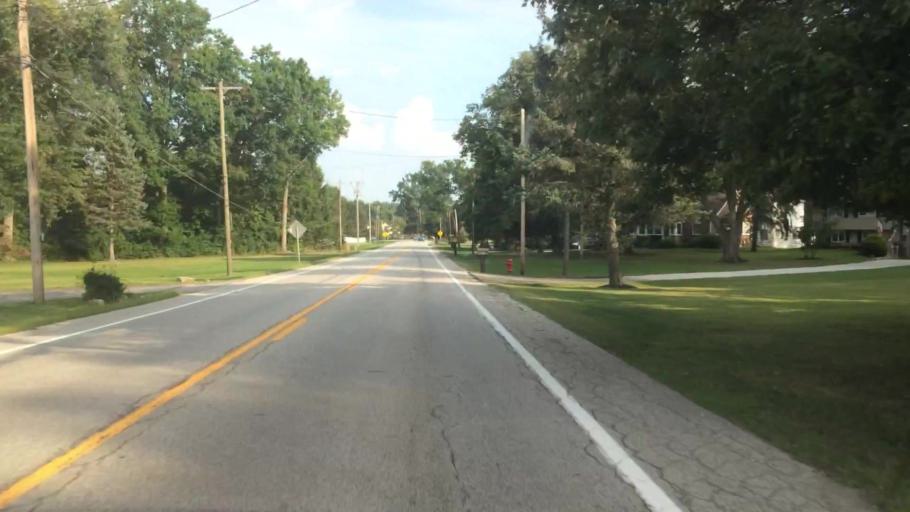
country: US
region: Ohio
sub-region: Cuyahoga County
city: Walton Hills
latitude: 41.3337
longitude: -81.5586
